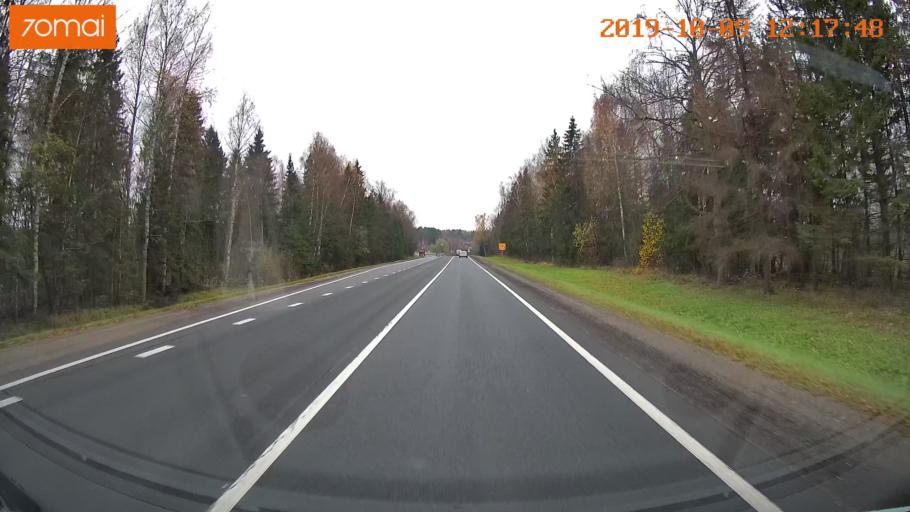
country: RU
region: Jaroslavl
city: Prechistoye
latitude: 58.4514
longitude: 40.3215
